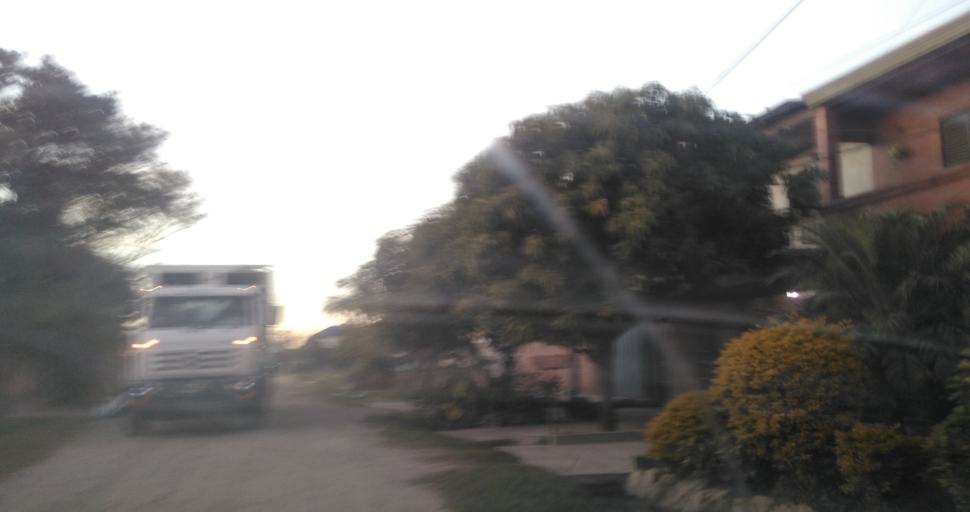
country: AR
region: Chaco
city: Resistencia
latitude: -27.4636
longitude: -59.0053
